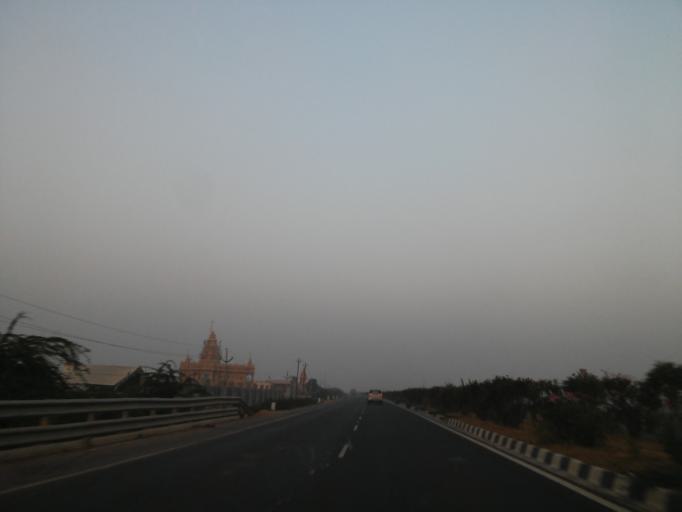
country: IN
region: Gujarat
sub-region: Surendranagar
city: Dhrangadhra
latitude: 23.0070
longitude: 71.3332
